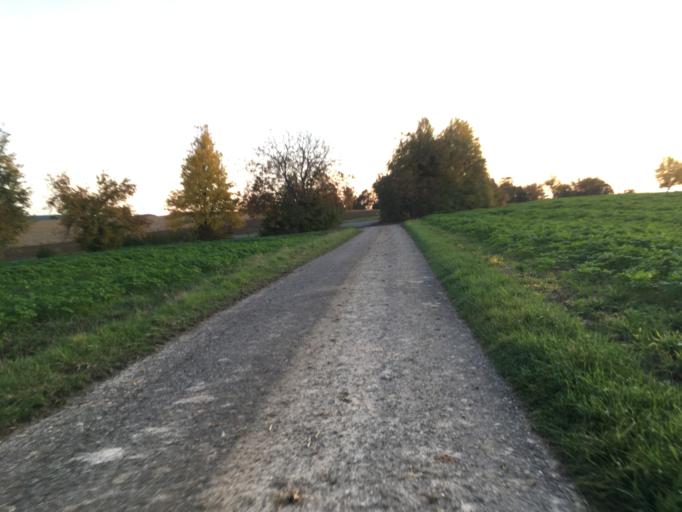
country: DE
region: Baden-Wuerttemberg
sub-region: Regierungsbezirk Stuttgart
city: Ohringen
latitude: 49.2137
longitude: 9.5344
